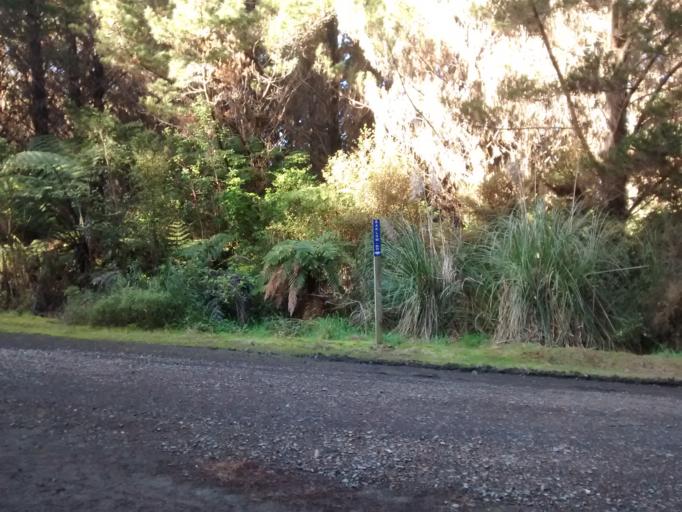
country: NZ
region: Auckland
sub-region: Auckland
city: Muriwai Beach
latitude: -36.7367
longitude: 174.5743
